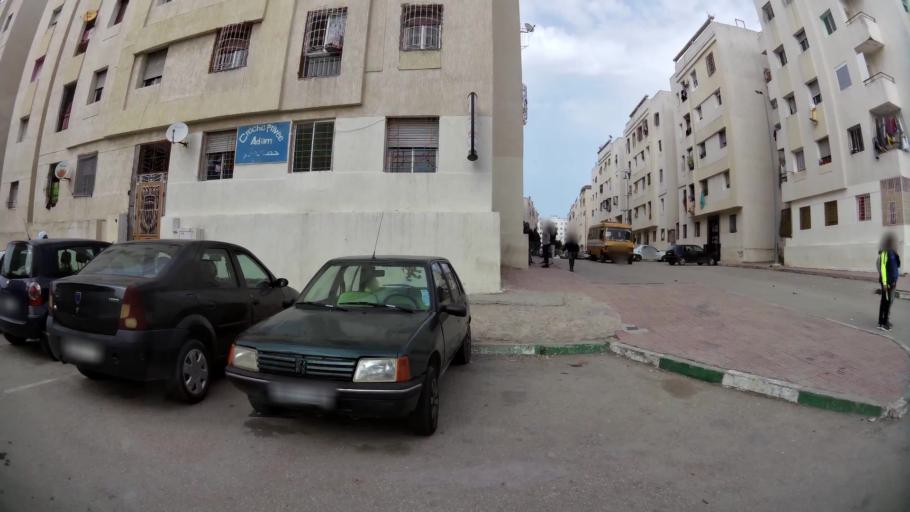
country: MA
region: Tanger-Tetouan
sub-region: Tanger-Assilah
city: Boukhalef
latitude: 35.7338
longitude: -5.8807
